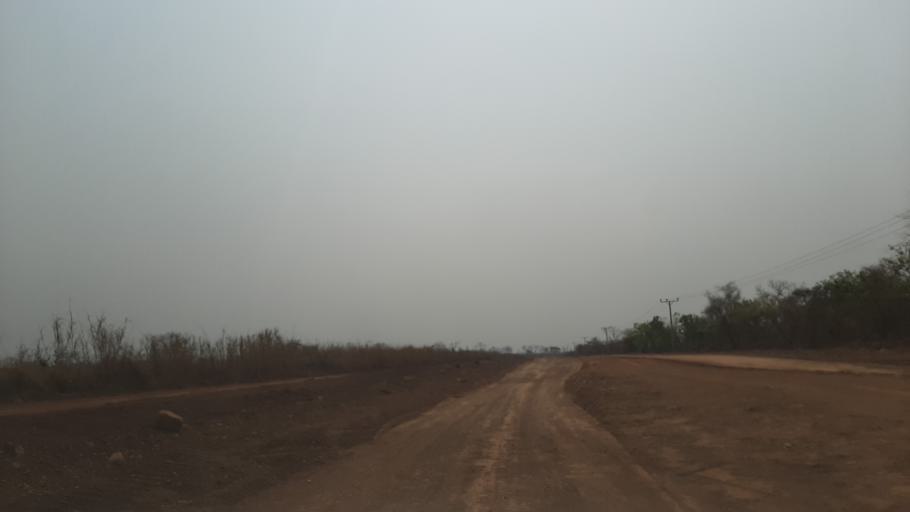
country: ET
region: Gambela
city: Gambela
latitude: 8.1594
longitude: 34.4665
